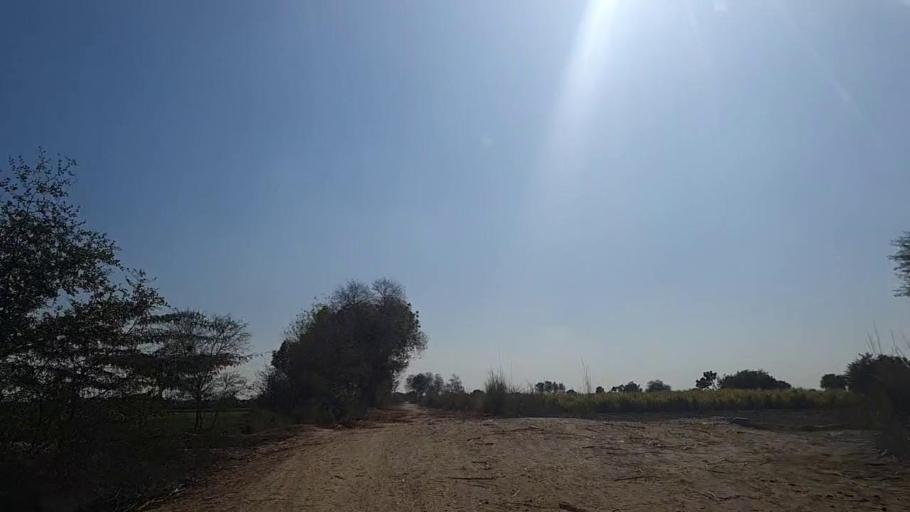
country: PK
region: Sindh
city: Sakrand
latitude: 26.2414
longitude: 68.1998
